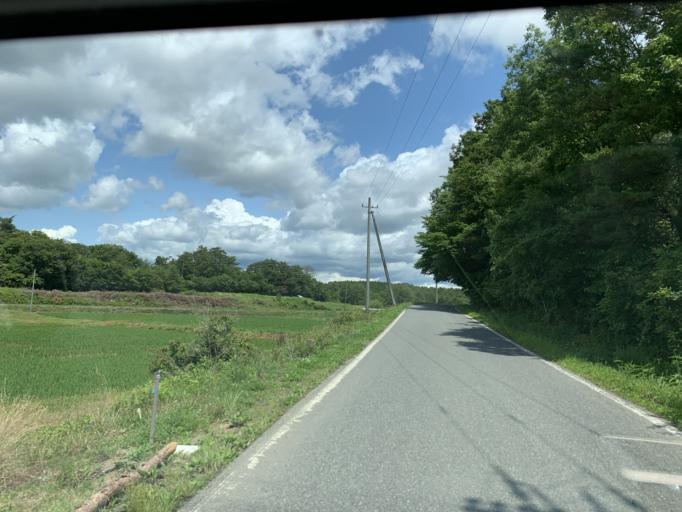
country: JP
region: Iwate
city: Ichinoseki
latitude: 38.9285
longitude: 141.0676
